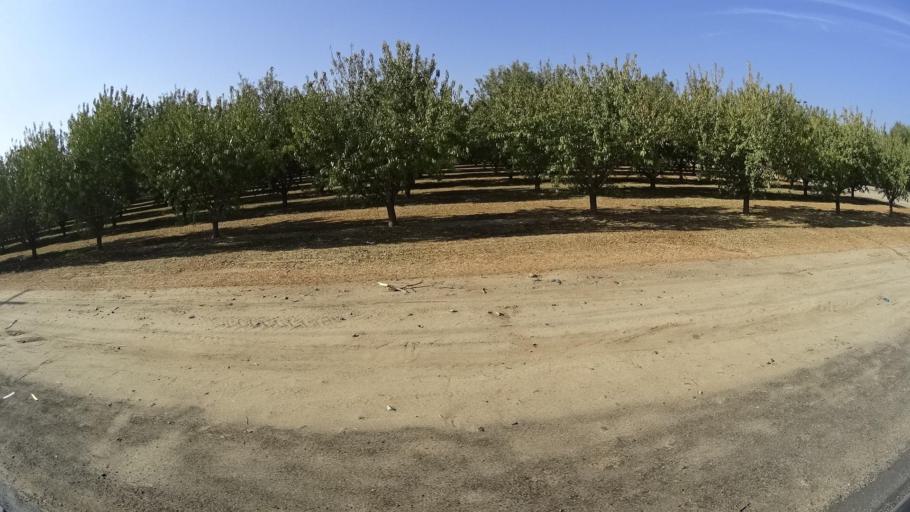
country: US
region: California
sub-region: Kern County
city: Shafter
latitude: 35.5030
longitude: -119.1524
